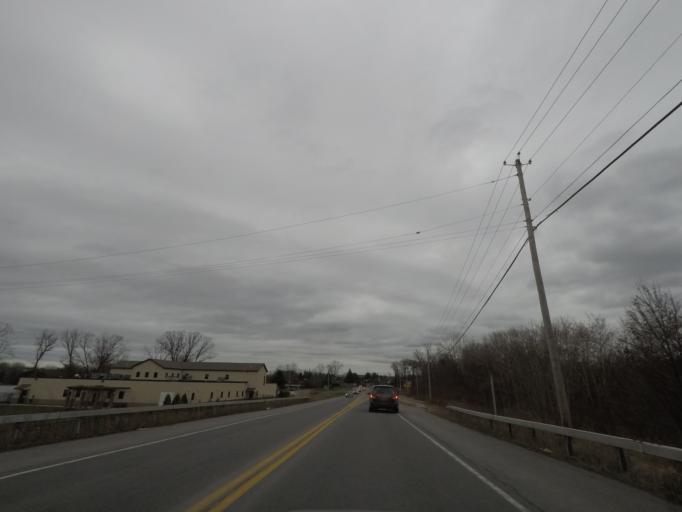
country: US
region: New York
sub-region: Albany County
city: Cohoes
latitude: 42.7592
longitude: -73.7631
